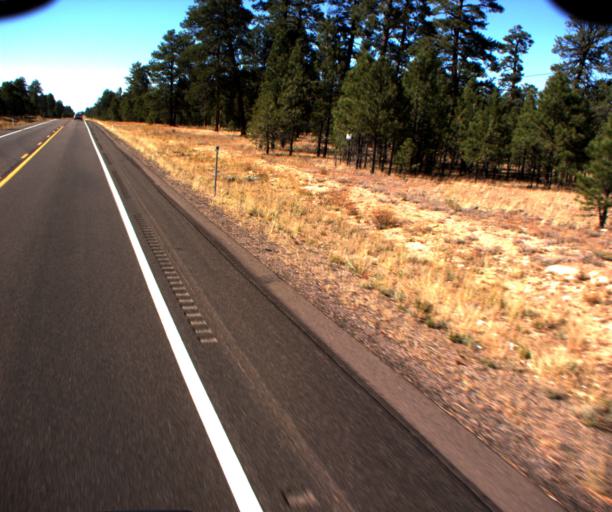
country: US
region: Arizona
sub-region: Apache County
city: Saint Michaels
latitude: 35.6881
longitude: -109.2475
